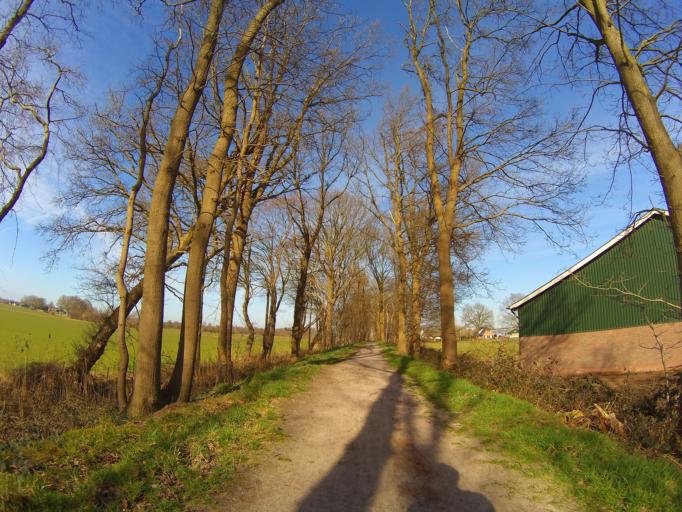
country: NL
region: Gelderland
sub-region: Gemeente Ede
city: Ederveen
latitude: 52.0741
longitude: 5.5616
